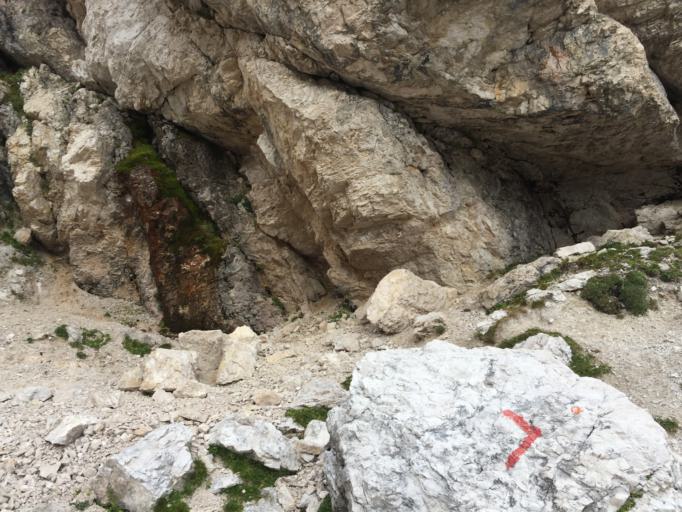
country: IT
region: Friuli Venezia Giulia
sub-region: Provincia di Udine
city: Malborghetto
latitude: 46.4274
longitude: 13.4965
